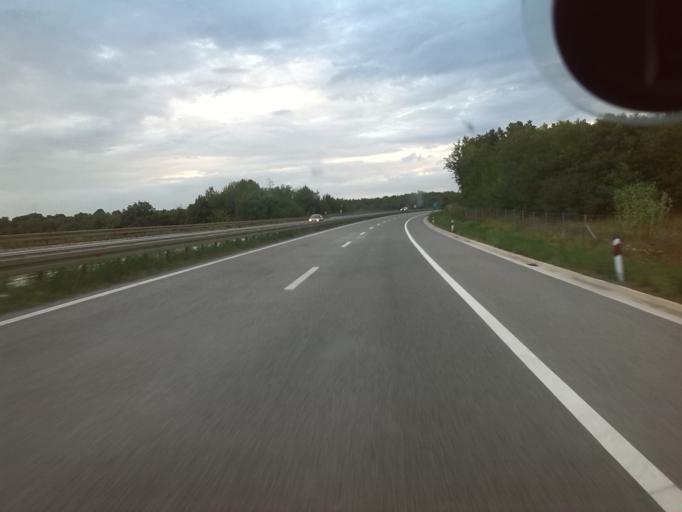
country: HR
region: Istarska
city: Buje
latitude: 45.3803
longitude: 13.6182
